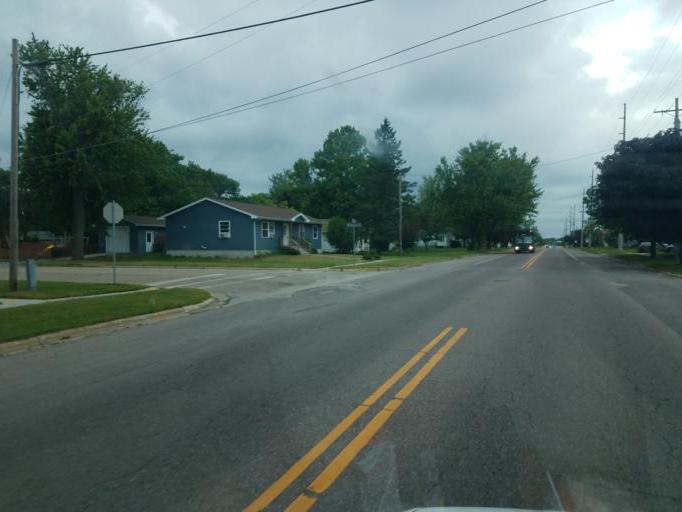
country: US
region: Wisconsin
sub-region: Juneau County
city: Mauston
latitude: 43.8010
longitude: -90.0699
